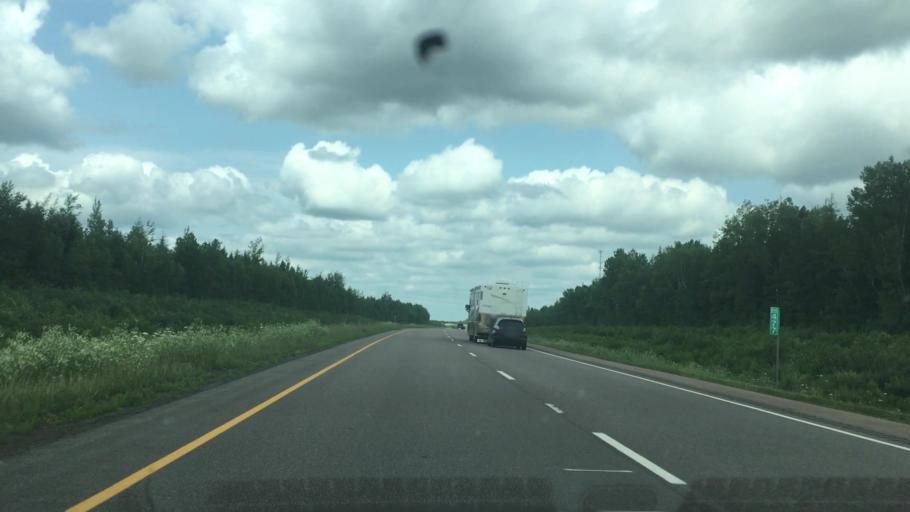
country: CA
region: New Brunswick
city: Dieppe
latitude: 46.0766
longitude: -64.5924
